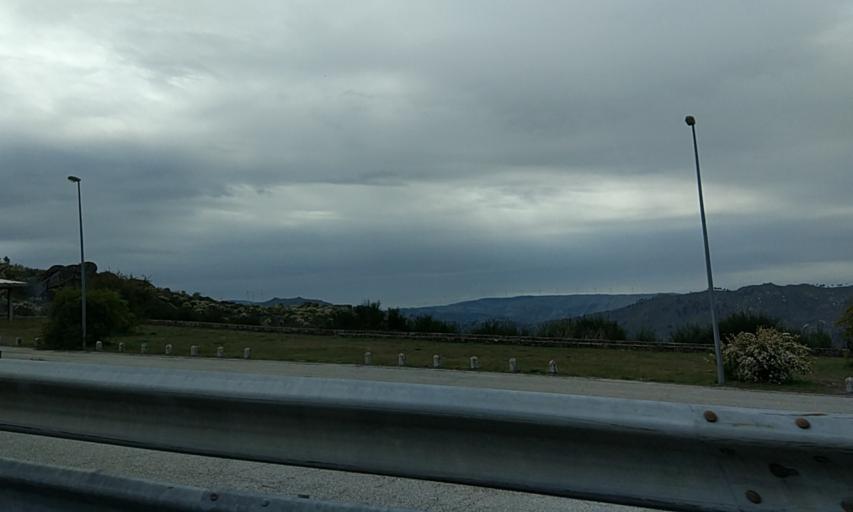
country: PT
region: Guarda
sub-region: Guarda
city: Guarda
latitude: 40.5900
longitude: -7.2748
